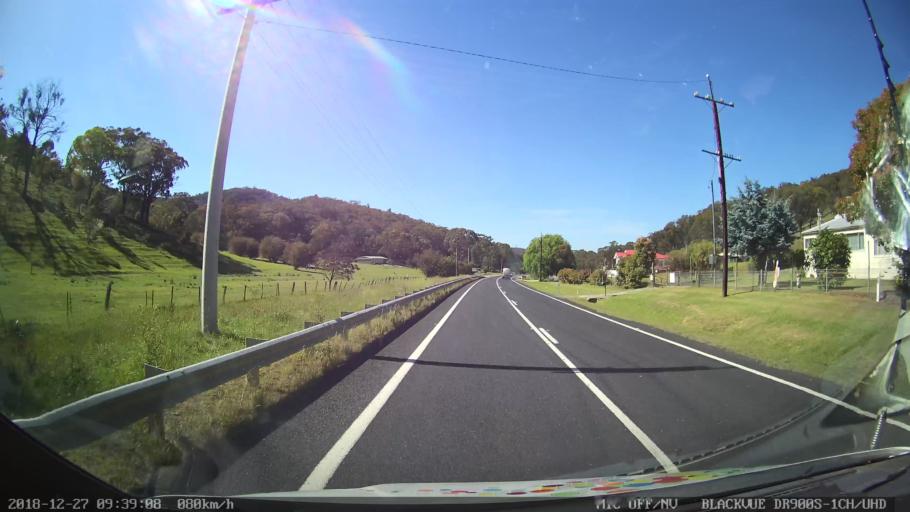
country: AU
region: New South Wales
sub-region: Lithgow
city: Portland
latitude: -33.2894
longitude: 150.0353
